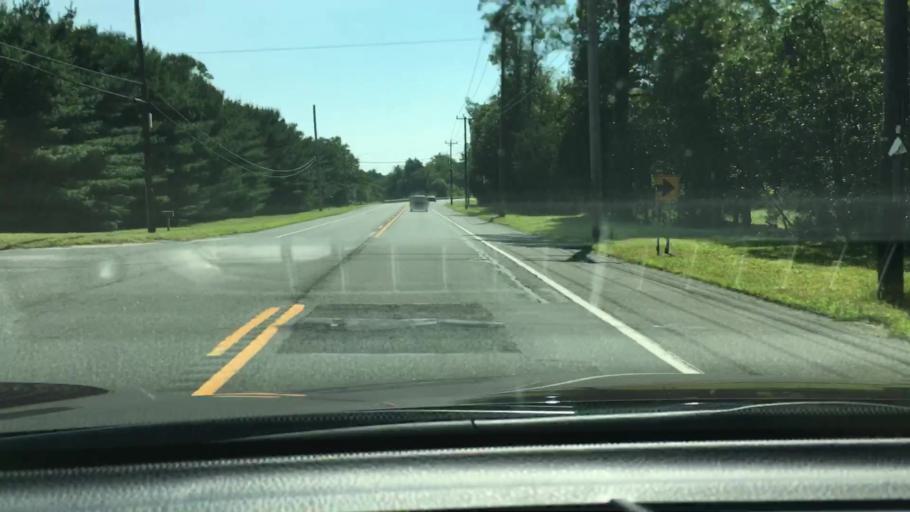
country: US
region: New Jersey
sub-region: Cumberland County
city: Laurel Lake
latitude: 39.3745
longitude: -74.9484
